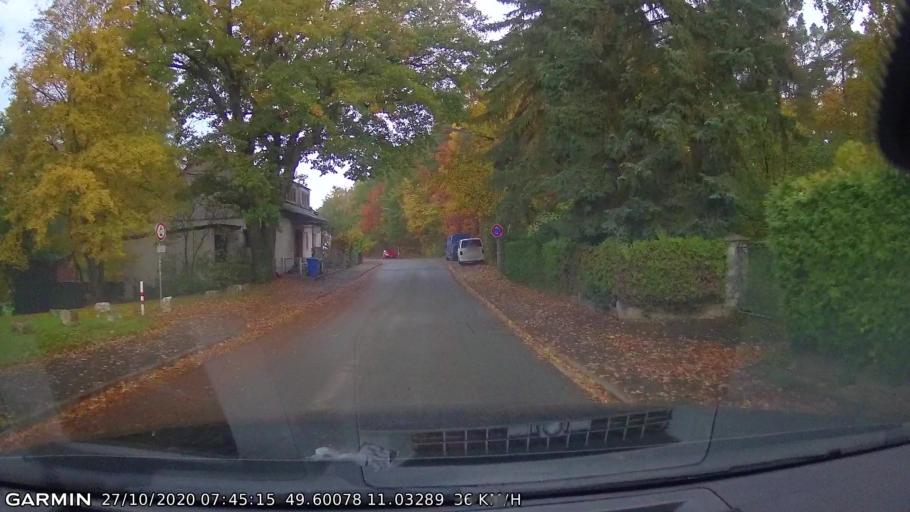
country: DE
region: Bavaria
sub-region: Regierungsbezirk Mittelfranken
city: Buckenhof
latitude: 49.6008
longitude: 11.0329
